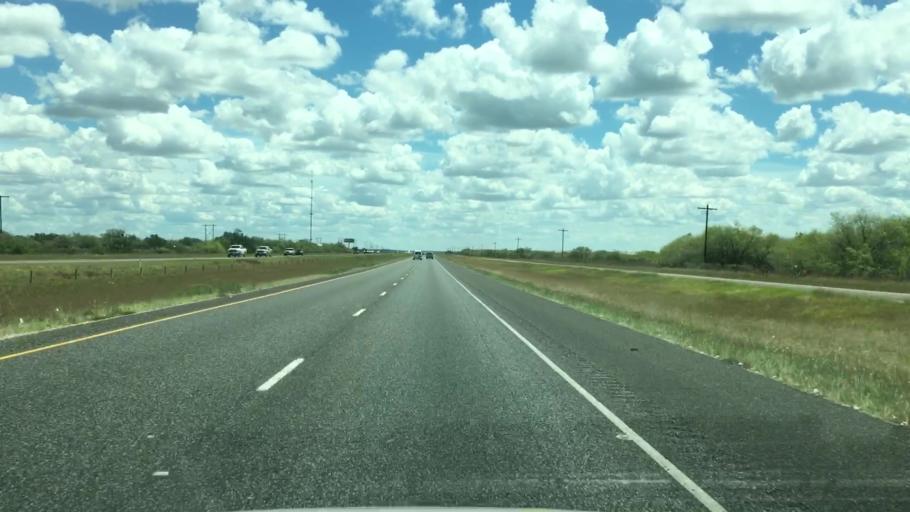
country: US
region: Texas
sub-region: Atascosa County
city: Pleasanton
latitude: 28.8078
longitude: -98.3492
